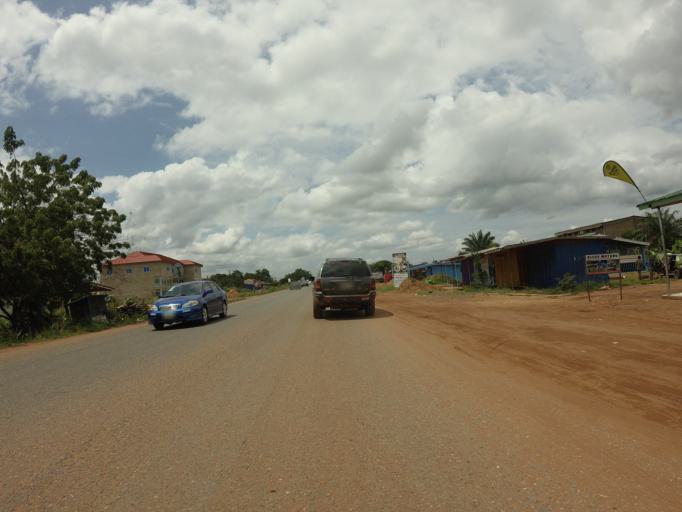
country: GH
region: Eastern
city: Aburi
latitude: 5.8401
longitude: -0.1160
